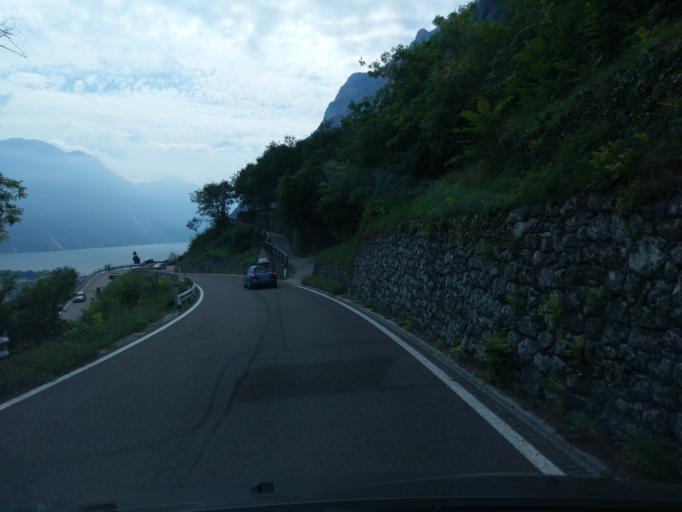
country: IT
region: Trentino-Alto Adige
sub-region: Provincia di Trento
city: Tenno
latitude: 45.9079
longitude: 10.8328
